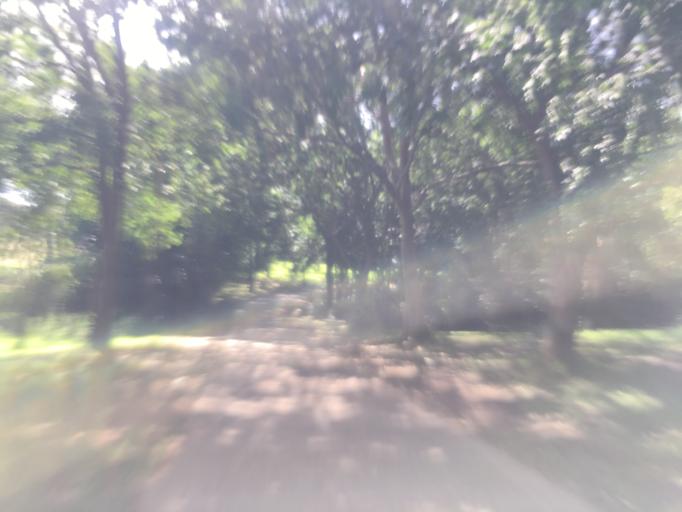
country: AU
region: New South Wales
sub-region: Camden
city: Elderslie
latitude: -34.0633
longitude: 150.6997
